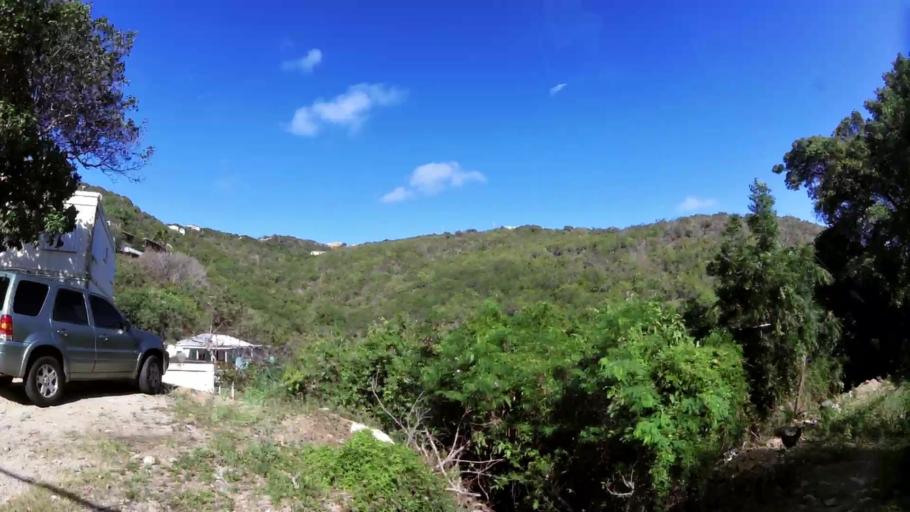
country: VG
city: Tortola
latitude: 18.4872
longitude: -64.3846
